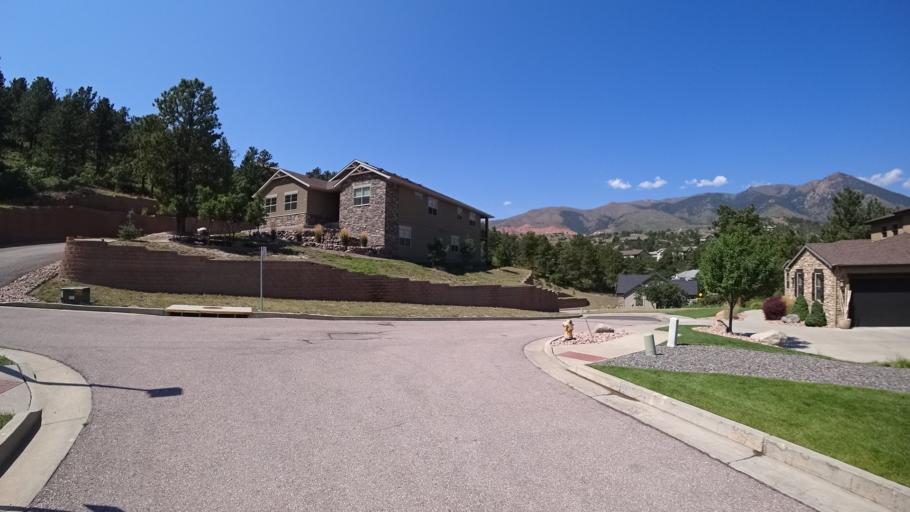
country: US
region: Colorado
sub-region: El Paso County
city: Air Force Academy
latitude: 38.9409
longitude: -104.8645
